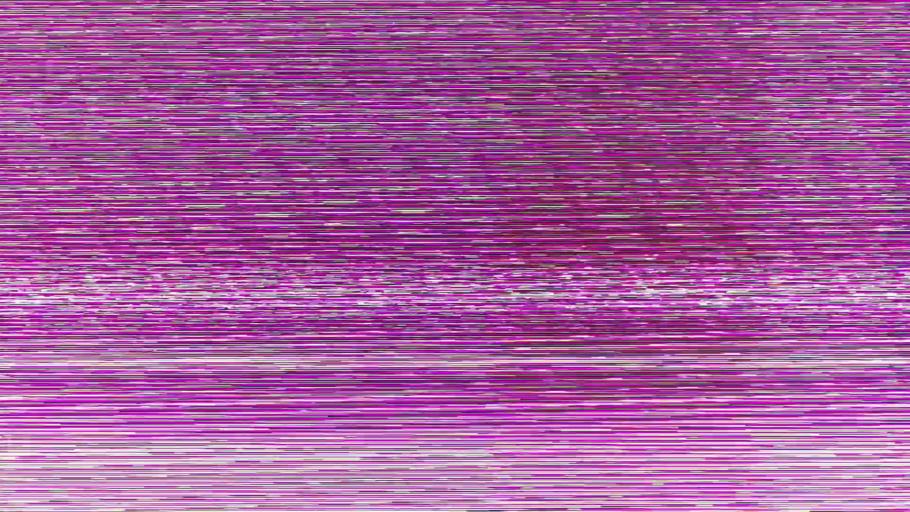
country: US
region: Michigan
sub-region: Wayne County
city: Wayne
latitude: 42.2876
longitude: -83.3803
